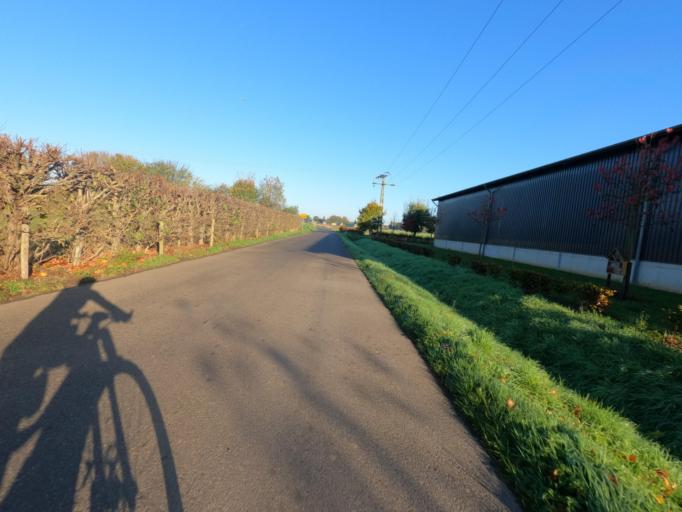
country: DE
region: North Rhine-Westphalia
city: Erkelenz
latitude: 51.0763
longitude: 6.3452
